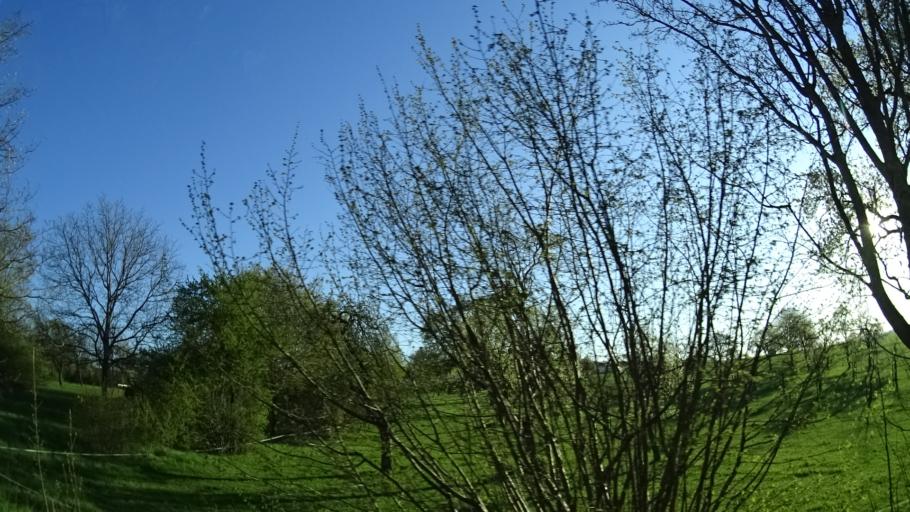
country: DE
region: Baden-Wuerttemberg
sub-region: Regierungsbezirk Stuttgart
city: Wolpertshausen
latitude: 49.1788
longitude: 9.8569
